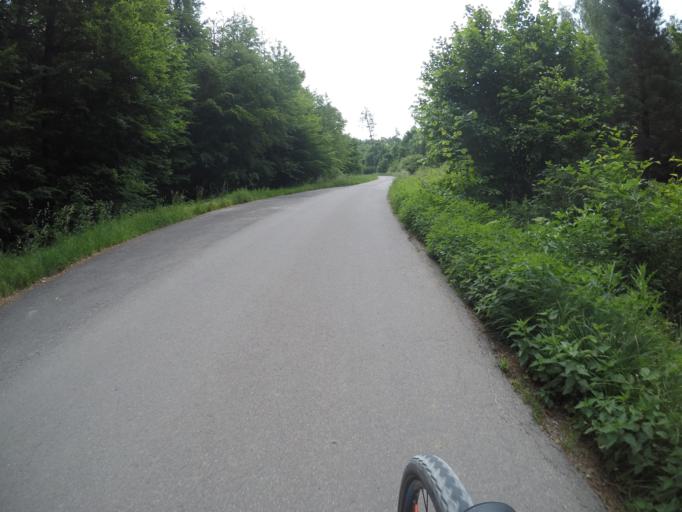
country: DE
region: Baden-Wuerttemberg
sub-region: Regierungsbezirk Stuttgart
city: Oberboihingen
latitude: 48.6488
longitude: 9.3974
